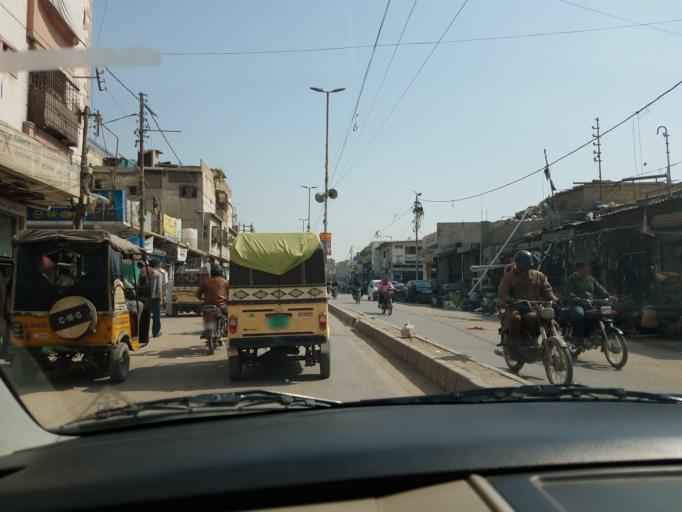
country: PK
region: Sindh
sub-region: Karachi District
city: Karachi
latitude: 24.8915
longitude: 67.0473
